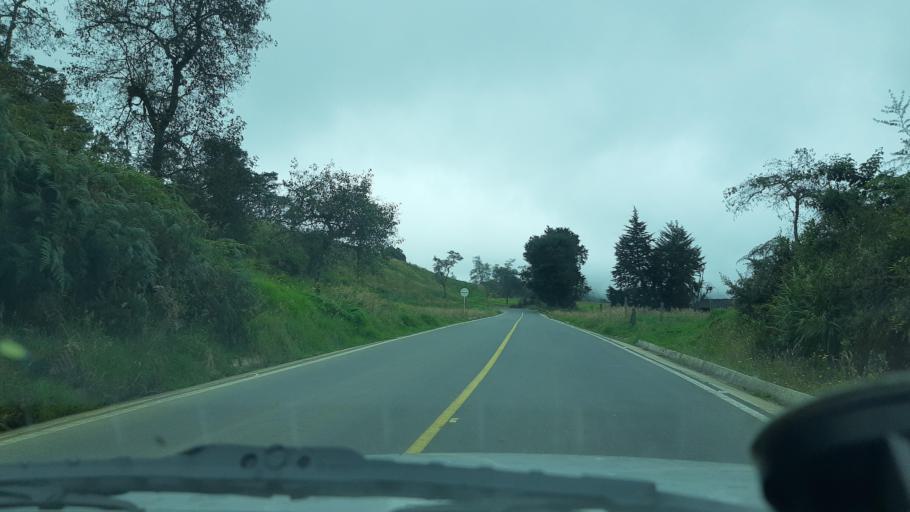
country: CO
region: Cundinamarca
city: Umbita
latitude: 5.2303
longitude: -73.4709
